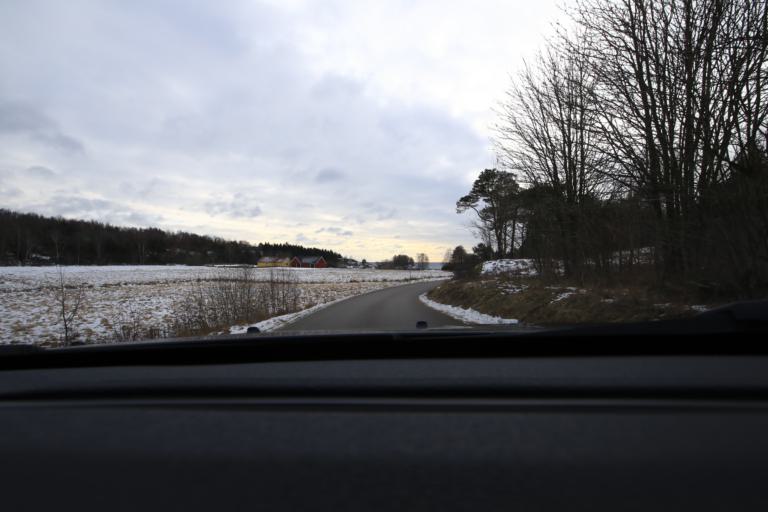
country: SE
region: Halland
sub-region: Kungsbacka Kommun
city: Frillesas
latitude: 57.2198
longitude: 12.1584
